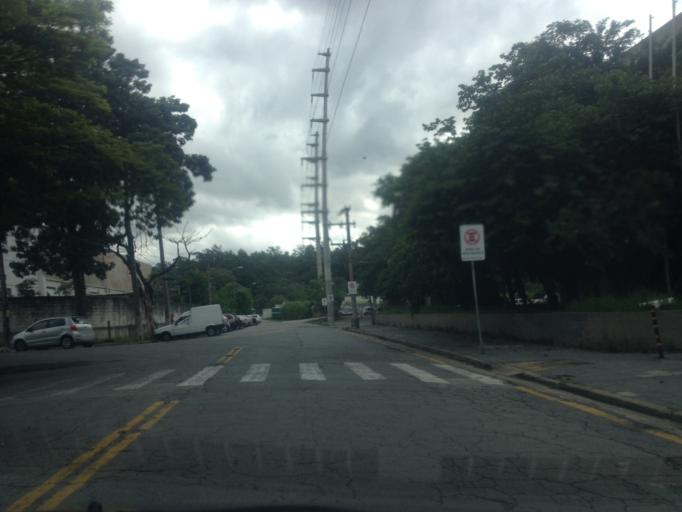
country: BR
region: Sao Paulo
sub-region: Sao Paulo
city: Sao Paulo
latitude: -23.5681
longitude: -46.7130
